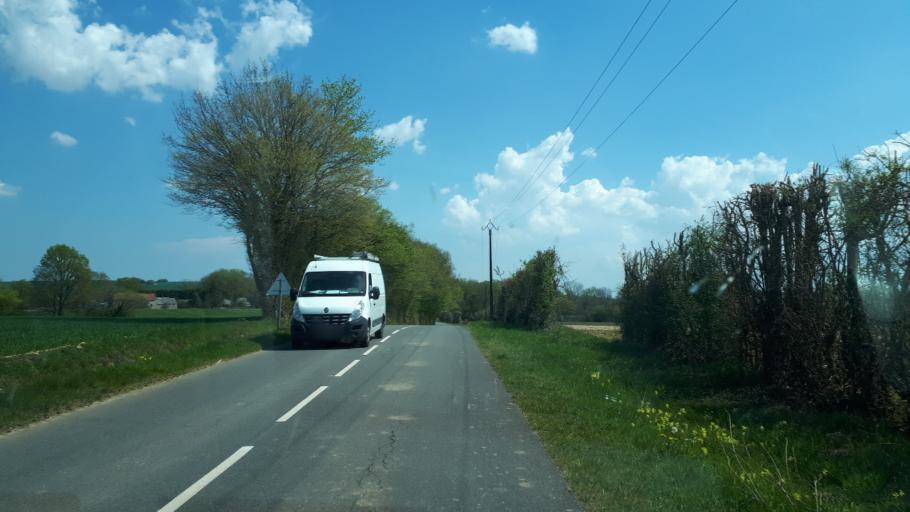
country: FR
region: Centre
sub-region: Departement du Cher
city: Sancerre
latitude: 47.3037
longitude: 2.6947
